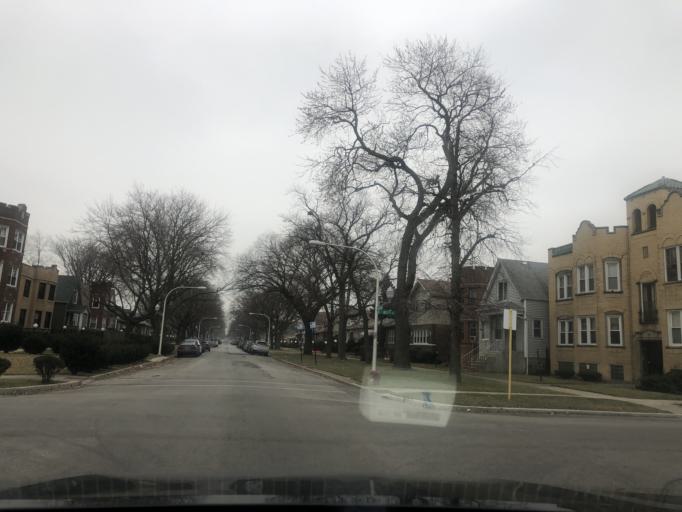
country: US
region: Illinois
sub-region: Cook County
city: Evergreen Park
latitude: 41.7494
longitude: -87.6198
